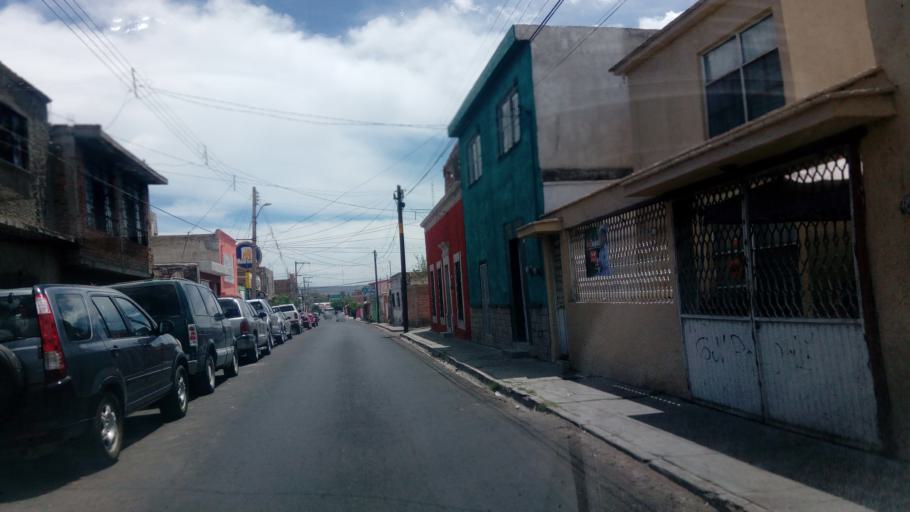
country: MX
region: Durango
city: Victoria de Durango
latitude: 24.0144
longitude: -104.6707
